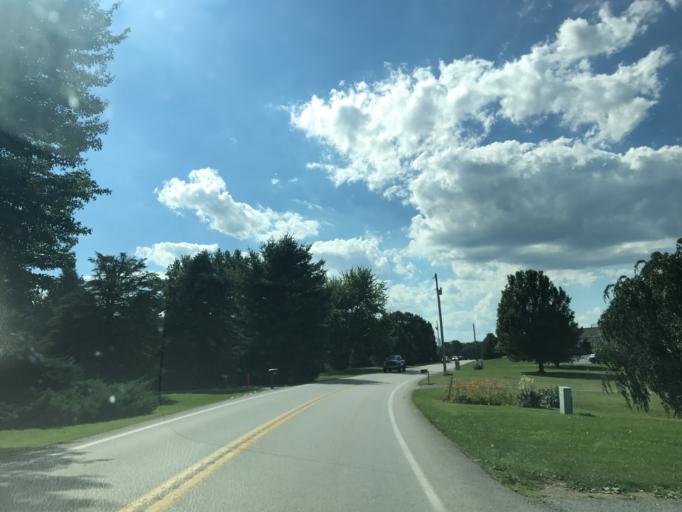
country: US
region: Pennsylvania
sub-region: York County
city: New Freedom
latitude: 39.7306
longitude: -76.7714
